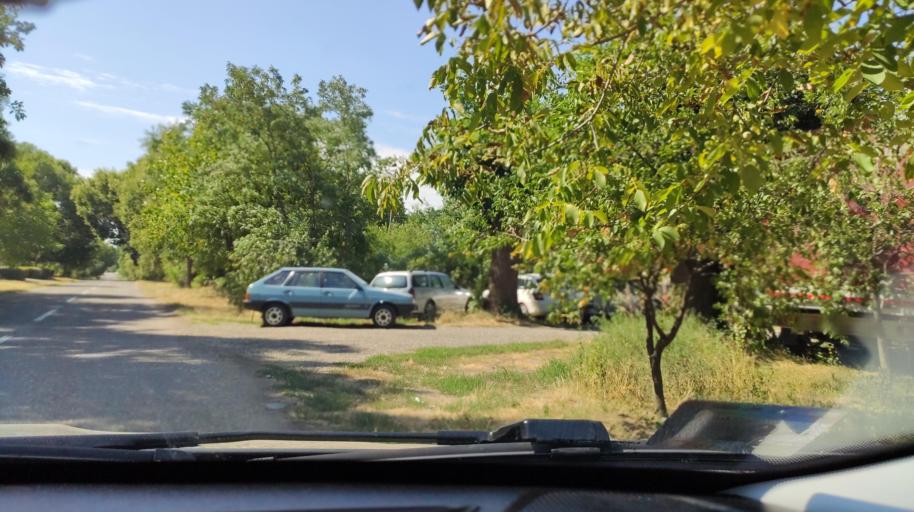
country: RS
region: Autonomna Pokrajina Vojvodina
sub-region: Severnobacki Okrug
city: Backa Topola
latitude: 45.8226
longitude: 19.6227
